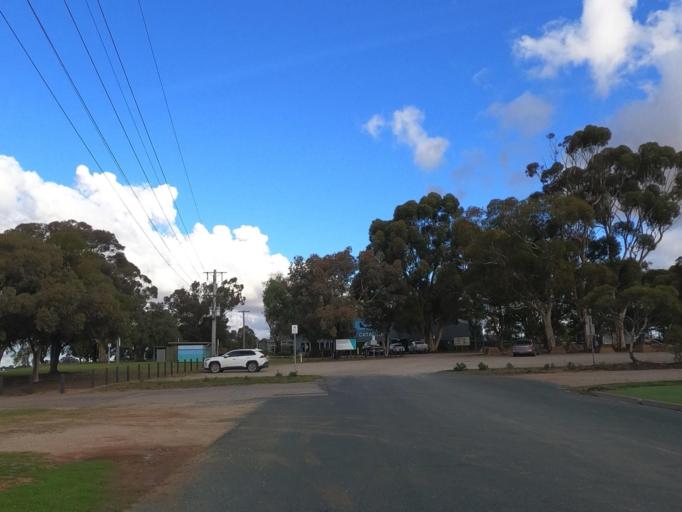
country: AU
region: Victoria
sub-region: Swan Hill
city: Swan Hill
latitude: -35.4497
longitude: 143.6275
